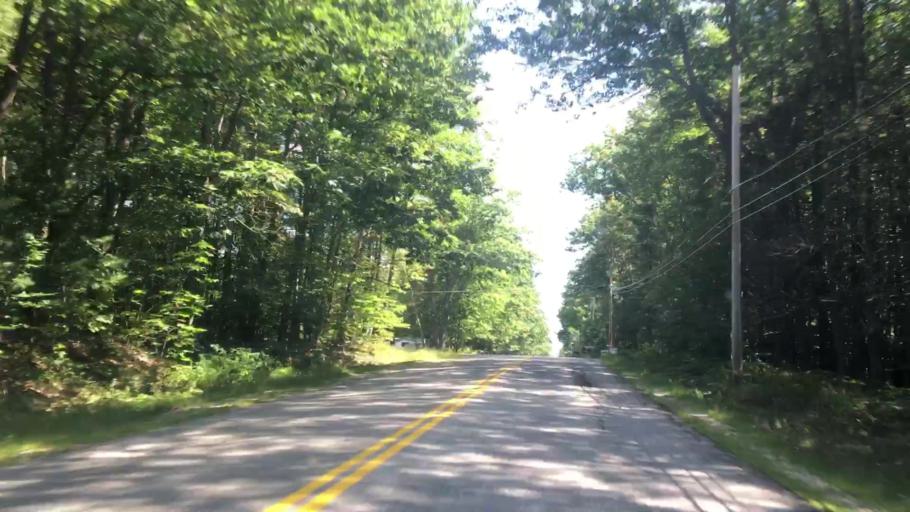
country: US
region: Maine
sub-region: Cumberland County
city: New Gloucester
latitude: 43.9382
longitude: -70.2920
